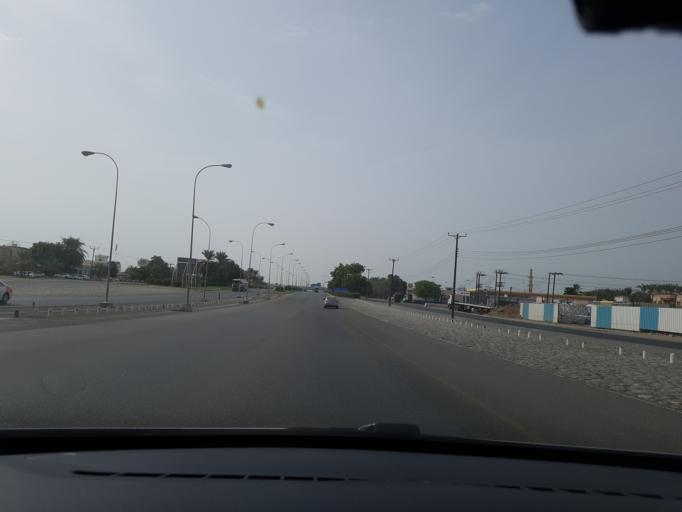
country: OM
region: Al Batinah
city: Al Sohar
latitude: 24.3544
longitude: 56.7129
